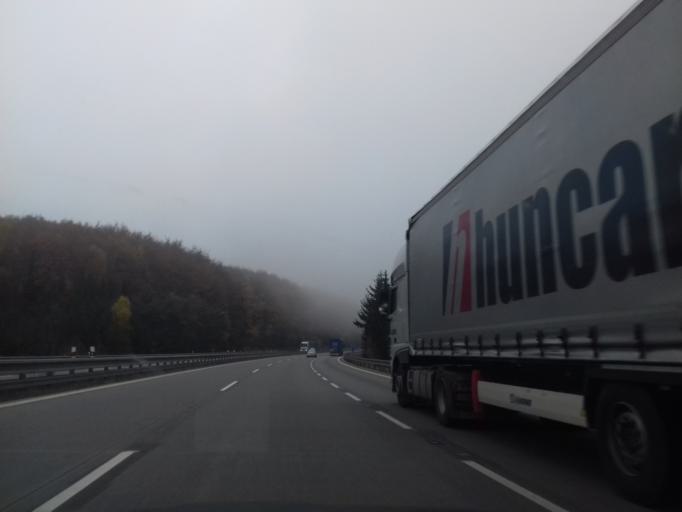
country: CZ
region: Vysocina
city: Stoky
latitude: 49.4694
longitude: 15.5696
